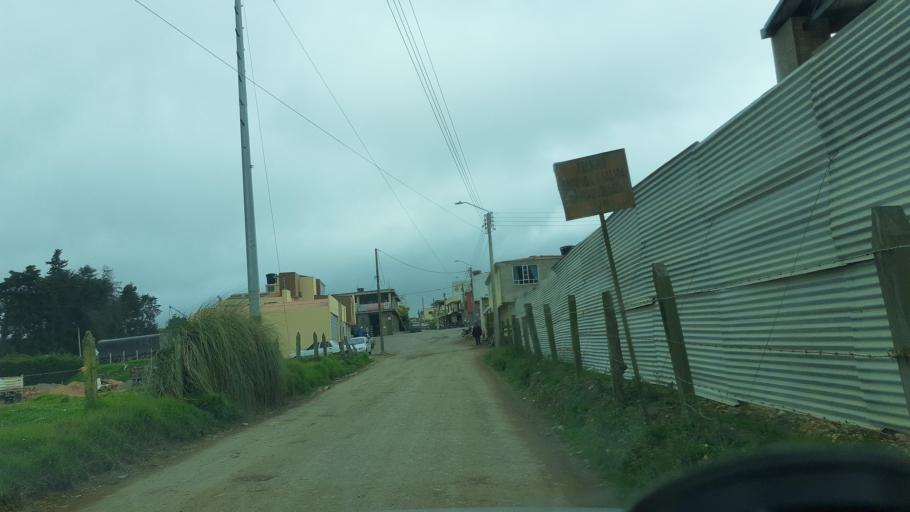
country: CO
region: Boyaca
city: Samaca
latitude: 5.4859
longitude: -73.4658
